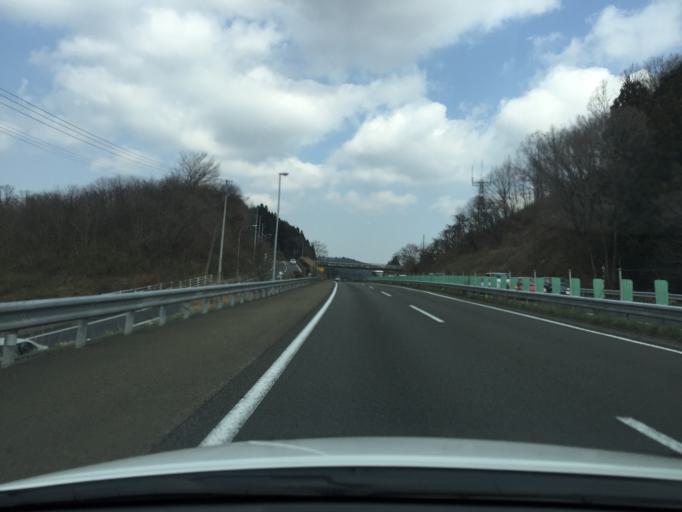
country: JP
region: Miyagi
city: Iwanuma
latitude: 38.1777
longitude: 140.7694
